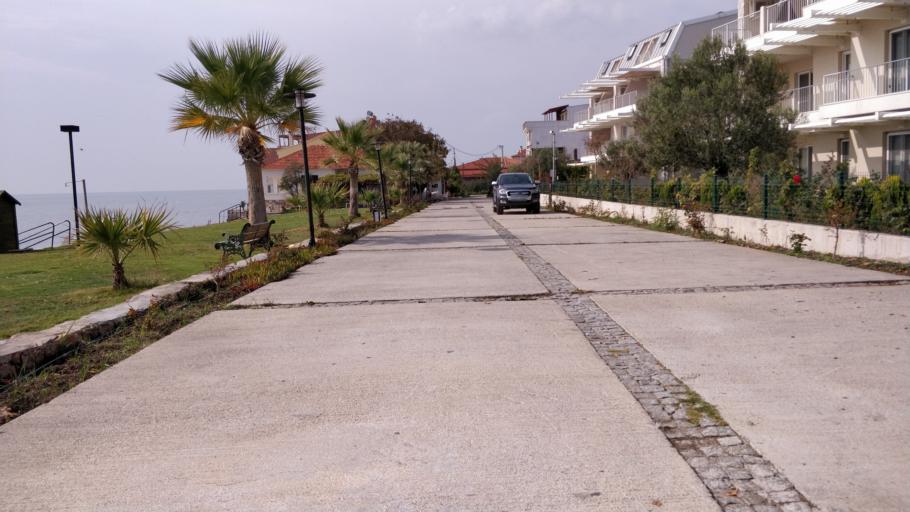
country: TR
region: Canakkale
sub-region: Merkez
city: Kucukkuyu
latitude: 39.5473
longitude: 26.6167
